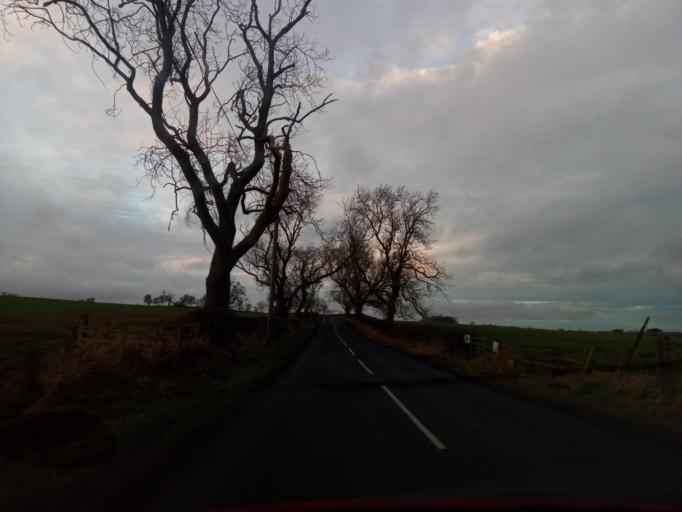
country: GB
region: England
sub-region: Northumberland
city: Ponteland
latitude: 55.1050
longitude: -1.7489
